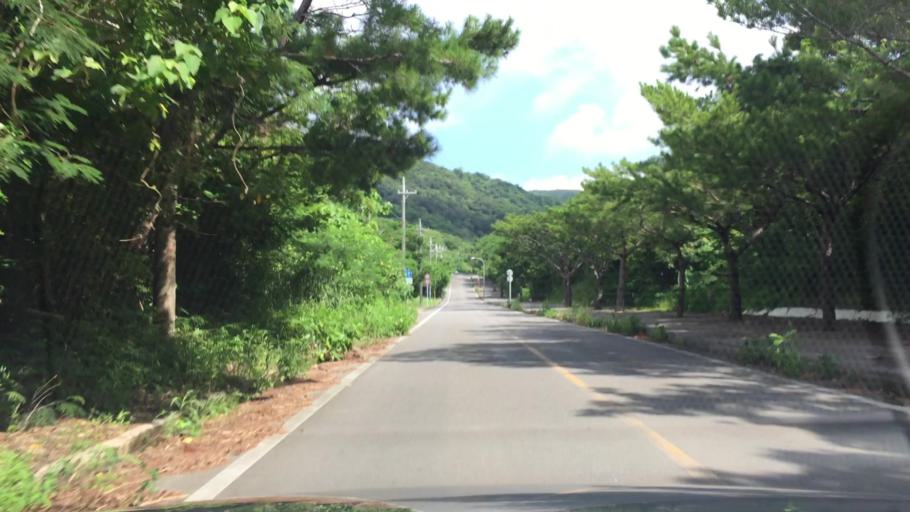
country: JP
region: Okinawa
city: Ishigaki
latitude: 24.4240
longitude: 124.2129
